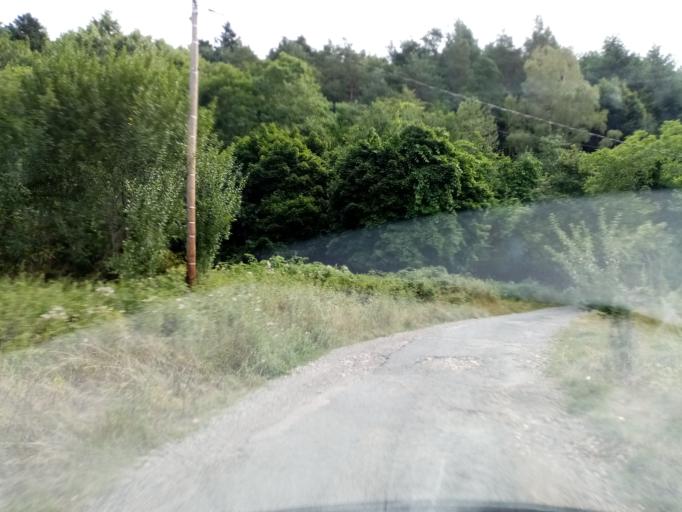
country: FR
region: Alsace
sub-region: Departement du Bas-Rhin
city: Ville
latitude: 48.3549
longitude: 7.3507
